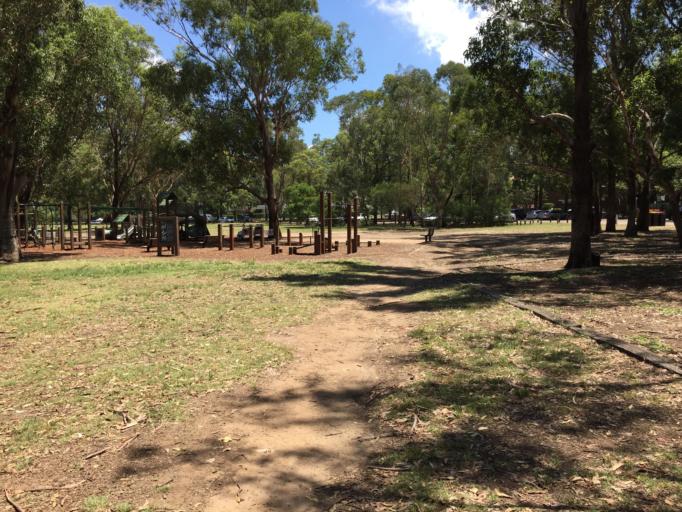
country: AU
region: New South Wales
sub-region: Parramatta
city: City of Parramatta
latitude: -33.8054
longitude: 150.9950
